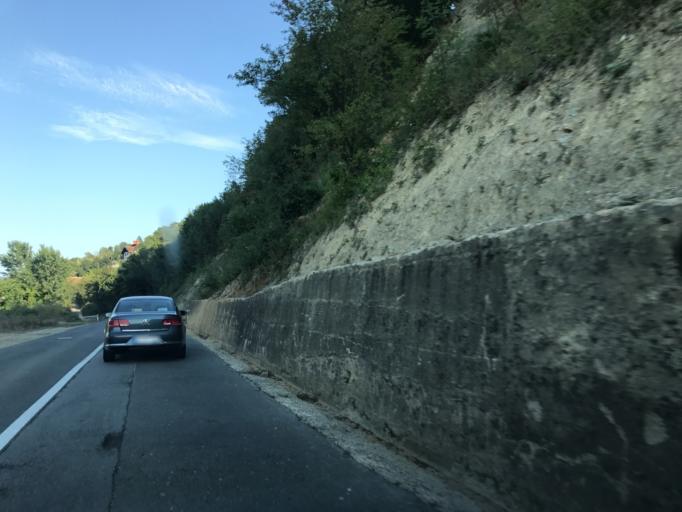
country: RO
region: Mehedinti
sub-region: Comuna Svinita
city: Svinita
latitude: 44.4737
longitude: 22.1084
